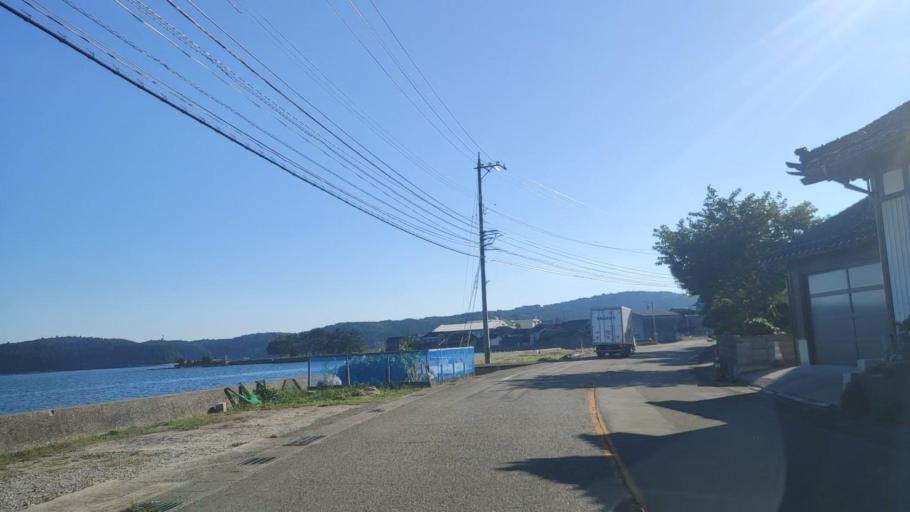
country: JP
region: Ishikawa
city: Nanao
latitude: 37.1518
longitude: 136.8794
